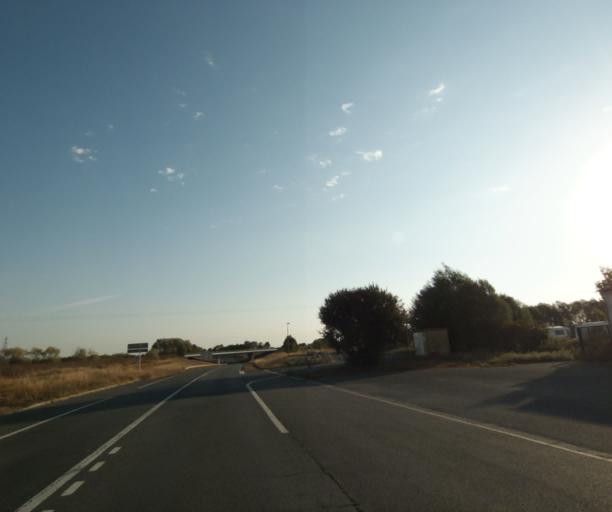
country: FR
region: Poitou-Charentes
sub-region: Departement de la Charente-Maritime
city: Breuil-Magne
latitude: 45.9561
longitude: -0.9346
